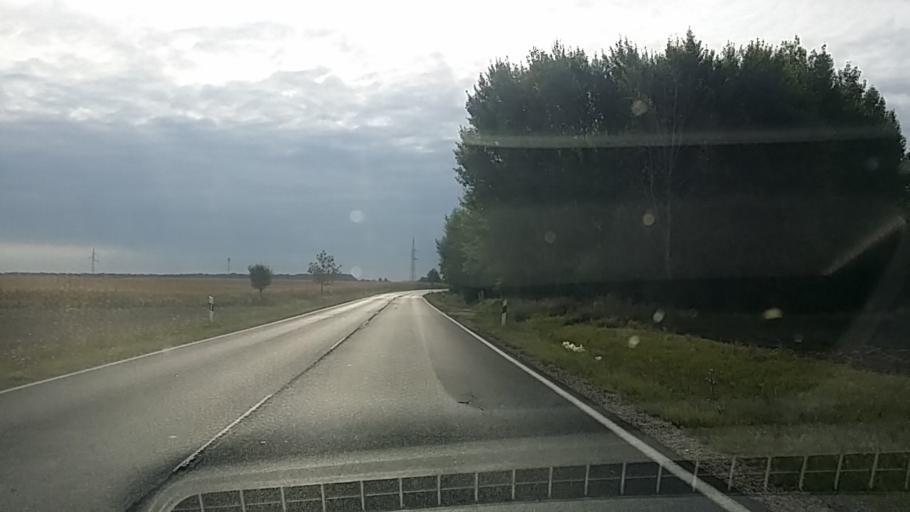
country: HU
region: Gyor-Moson-Sopron
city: Fertoszentmiklos
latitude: 47.5953
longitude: 16.9332
